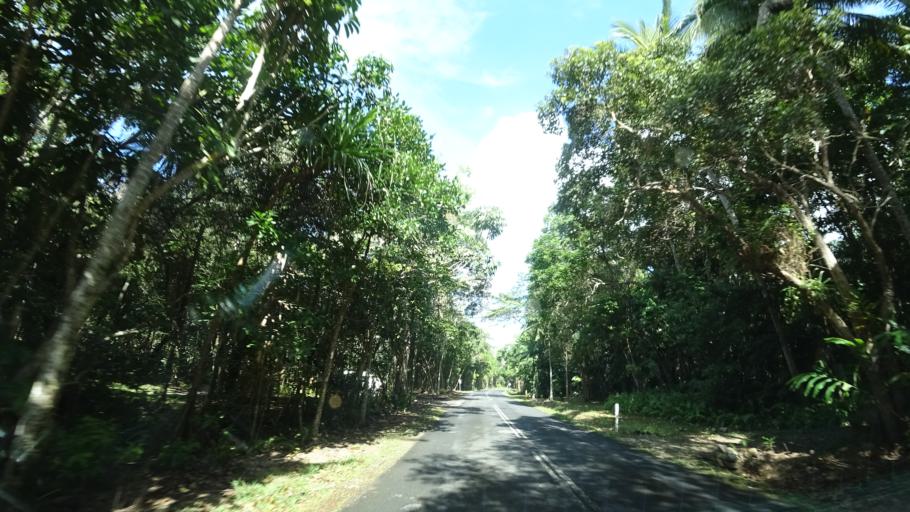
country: AU
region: Queensland
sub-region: Cairns
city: Port Douglas
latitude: -16.1734
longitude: 145.4410
